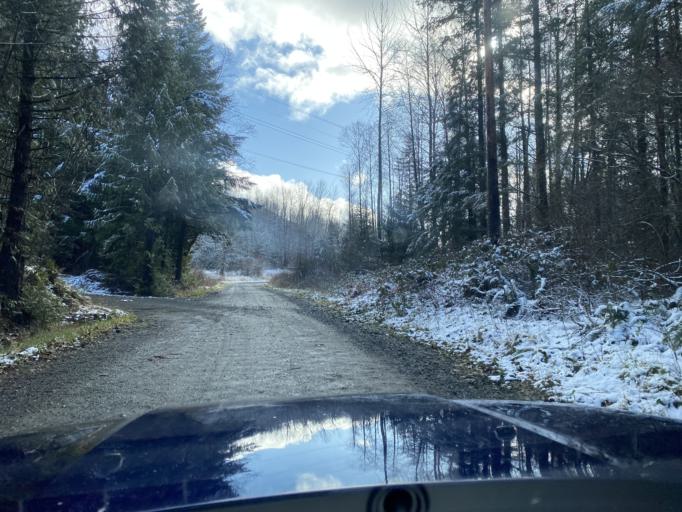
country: US
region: Washington
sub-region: King County
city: Snoqualmie
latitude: 47.4968
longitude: -121.8743
